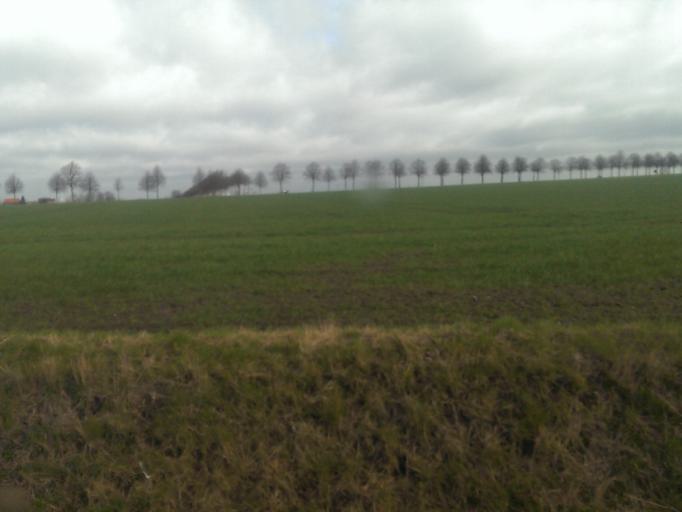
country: DE
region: Lower Saxony
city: Schellerten
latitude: 52.1708
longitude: 10.0436
